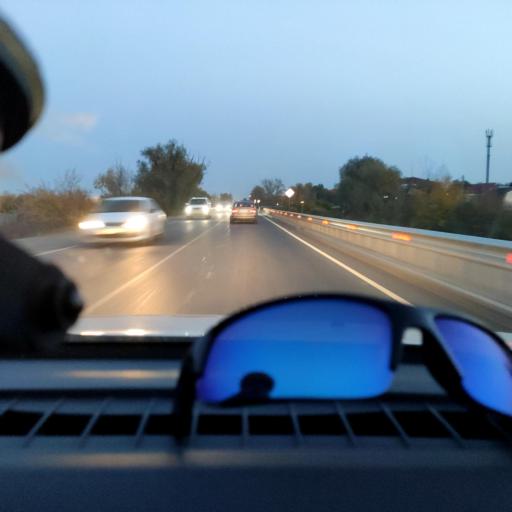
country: RU
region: Samara
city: Samara
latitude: 53.1204
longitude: 50.1202
